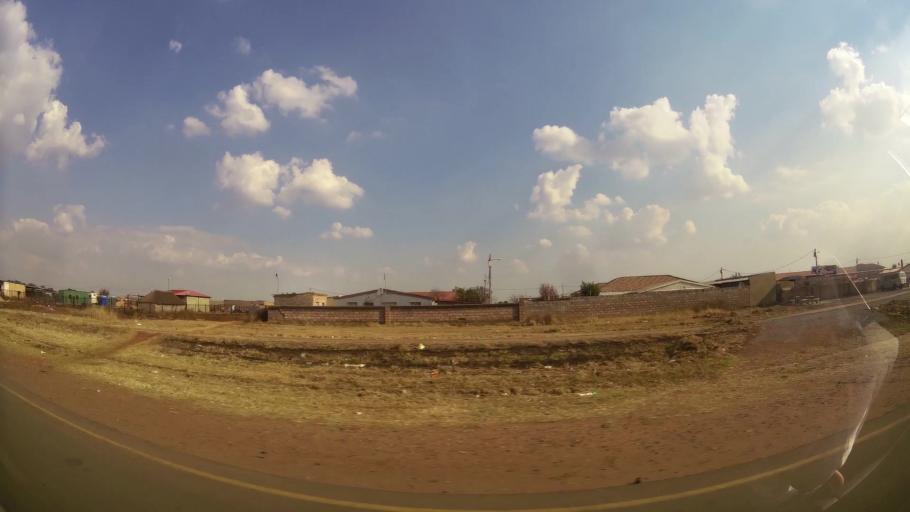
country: ZA
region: Gauteng
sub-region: Ekurhuleni Metropolitan Municipality
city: Germiston
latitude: -26.3151
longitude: 28.2075
